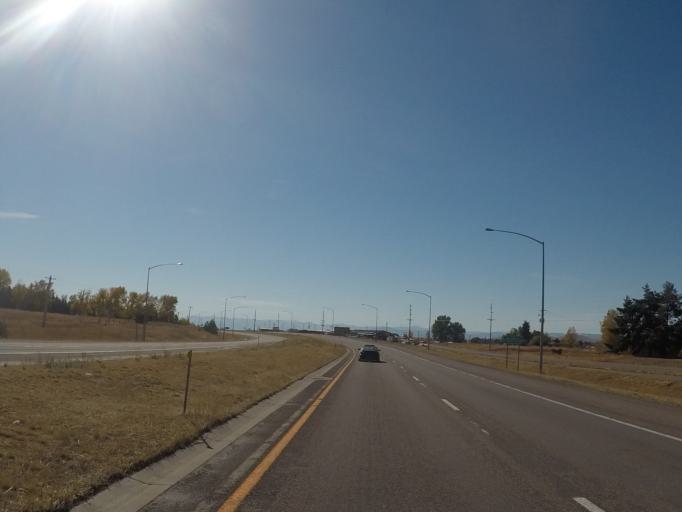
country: US
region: Montana
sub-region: Lake County
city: Polson
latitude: 47.6641
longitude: -114.1113
